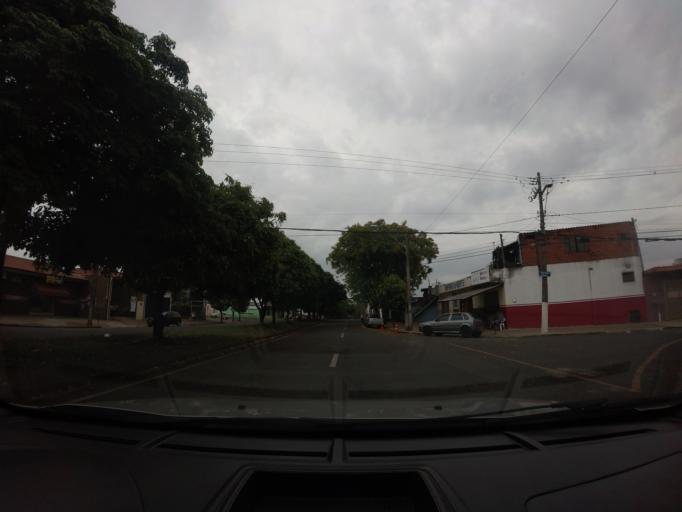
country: BR
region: Sao Paulo
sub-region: Piracicaba
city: Piracicaba
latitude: -22.7665
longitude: -47.5891
